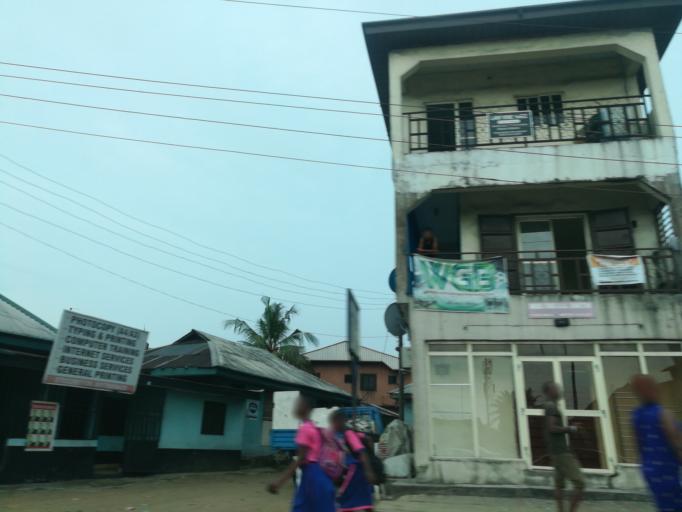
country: NG
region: Rivers
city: Port Harcourt
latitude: 4.8155
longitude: 7.0225
